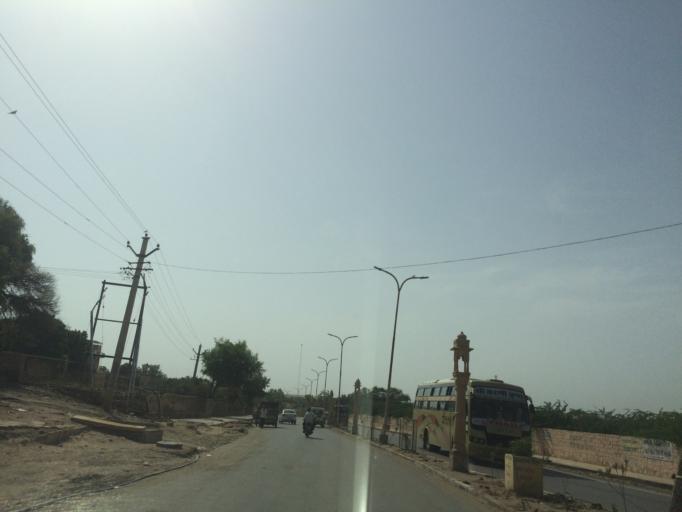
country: IN
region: Rajasthan
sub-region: Jaisalmer
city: Jaisalmer
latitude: 26.9103
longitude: 70.9102
